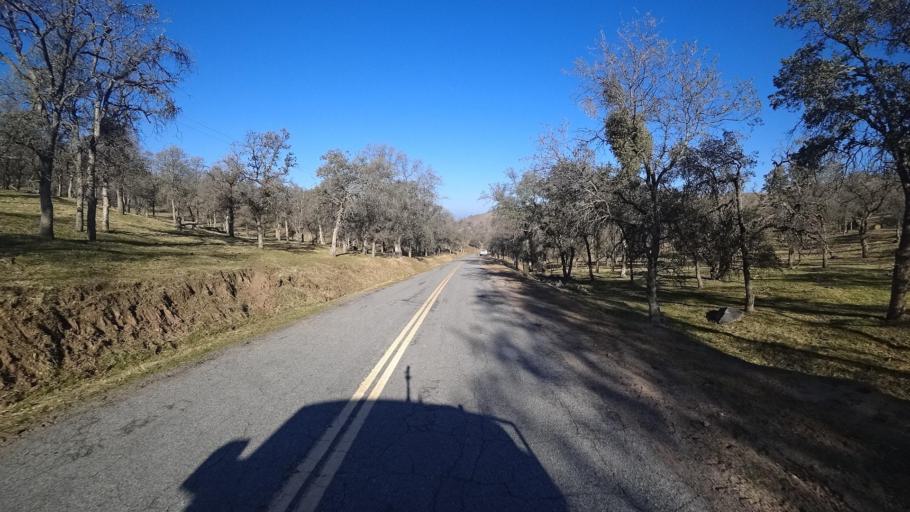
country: US
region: California
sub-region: Kern County
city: Alta Sierra
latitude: 35.7643
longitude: -118.8210
